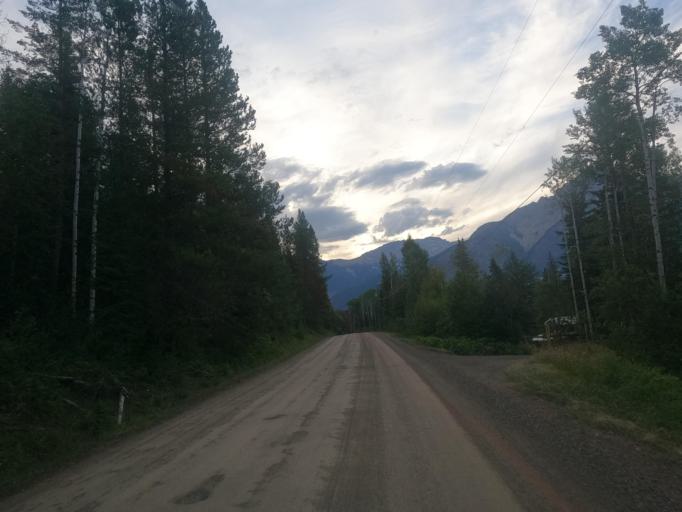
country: CA
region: British Columbia
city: Golden
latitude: 51.4444
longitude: -117.0282
